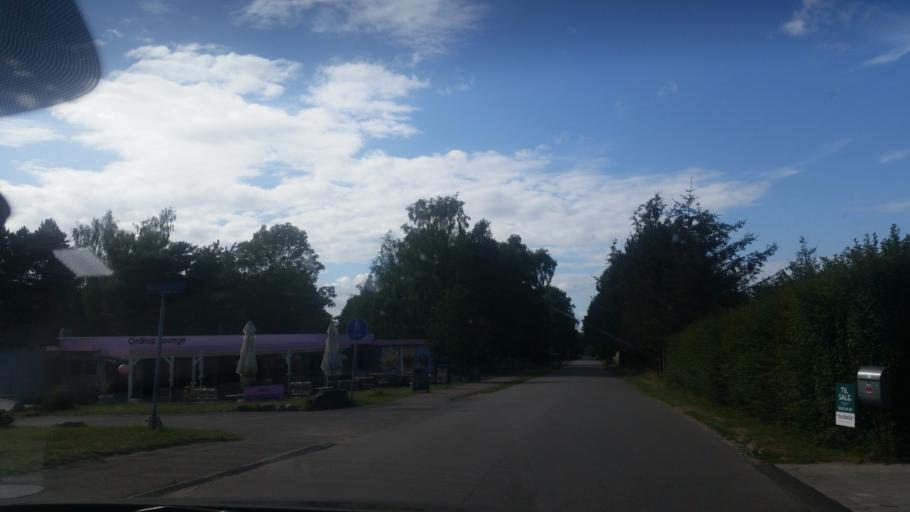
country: DK
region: Zealand
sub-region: Odsherred Kommune
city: Horve
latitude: 55.8237
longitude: 11.4022
